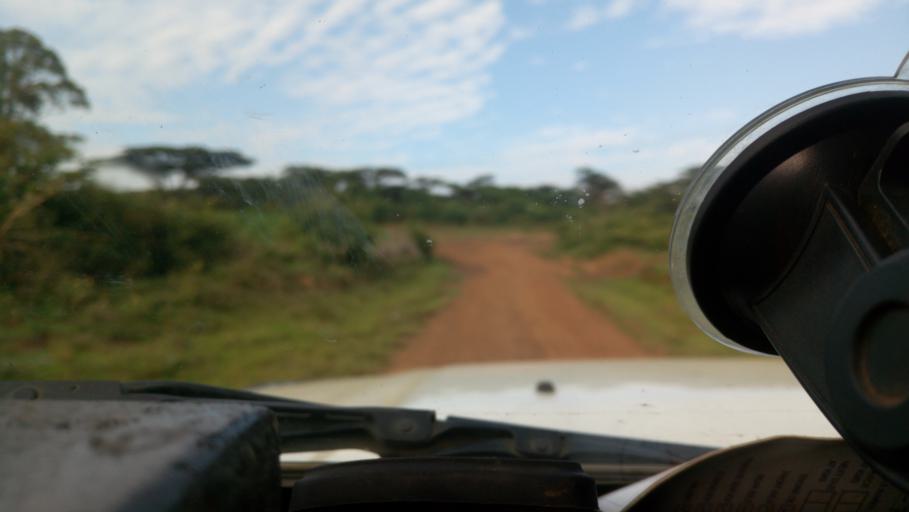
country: KE
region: Kericho
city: Londiani
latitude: -0.1844
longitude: 35.5902
